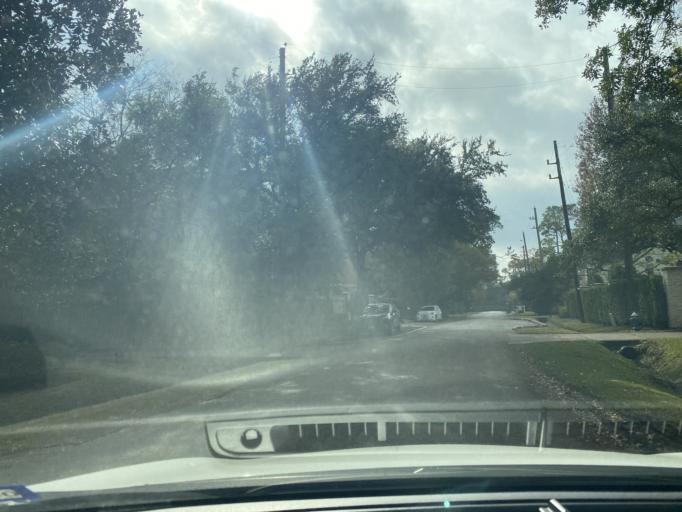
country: US
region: Texas
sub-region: Harris County
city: Hunters Creek Village
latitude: 29.7656
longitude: -95.4727
